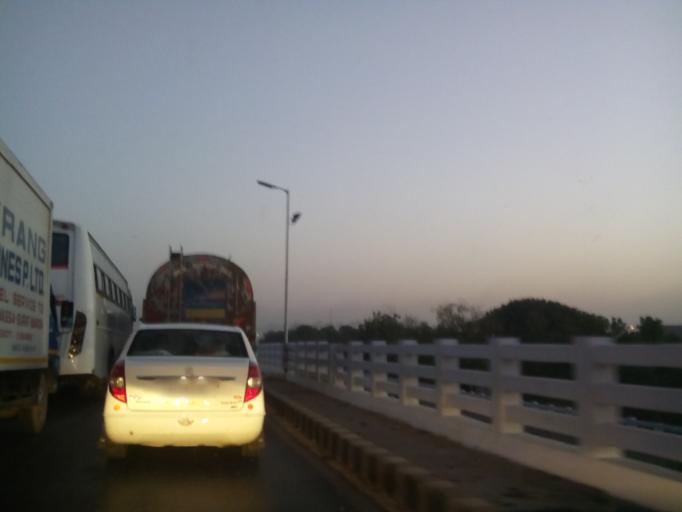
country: IN
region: Gujarat
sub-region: Mahesana
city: Visnagar
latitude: 23.5770
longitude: 72.3674
